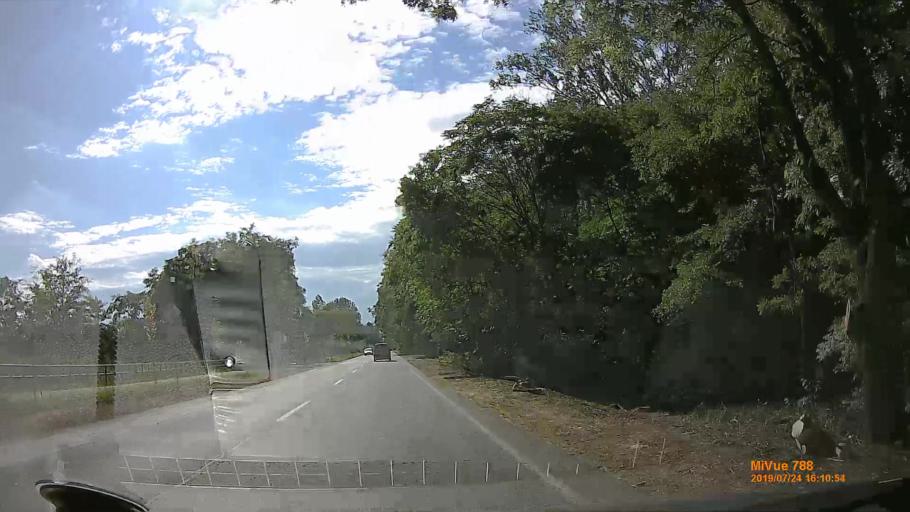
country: HU
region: Szabolcs-Szatmar-Bereg
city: Napkor
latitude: 47.9498
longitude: 21.8425
